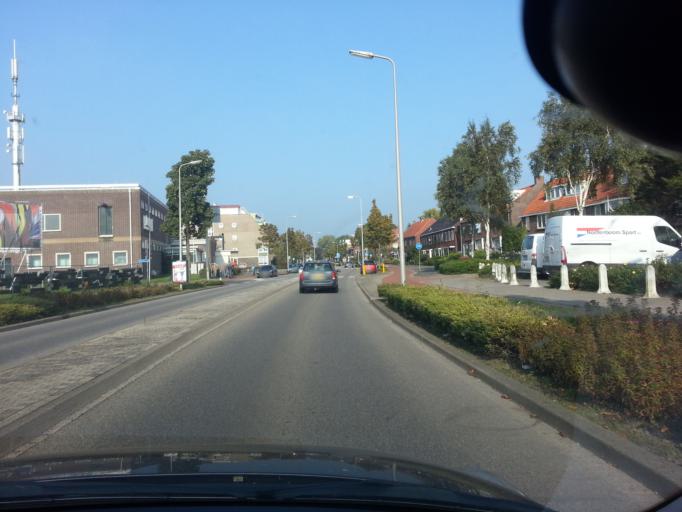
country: NL
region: South Holland
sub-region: Gemeente Zwijndrecht
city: Zwijndrecht
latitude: 51.8195
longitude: 4.6448
